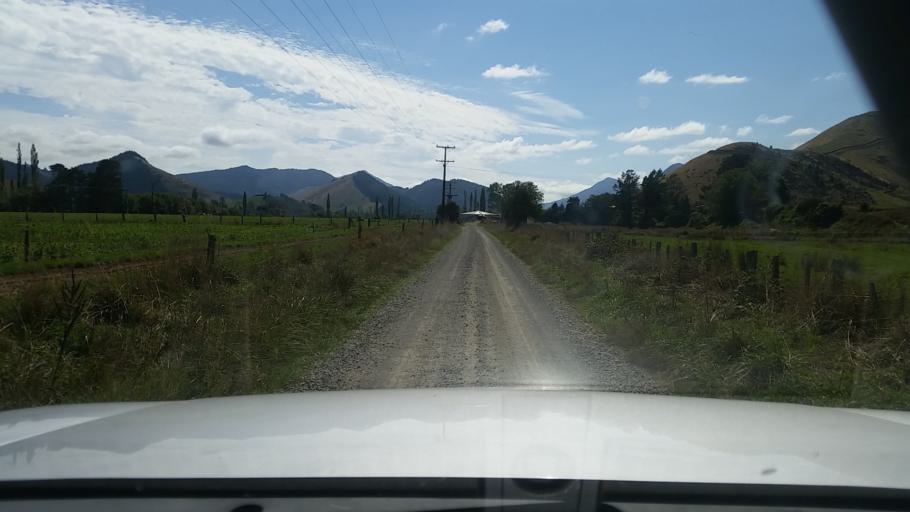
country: NZ
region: Nelson
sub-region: Nelson City
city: Nelson
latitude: -41.2517
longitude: 173.5830
